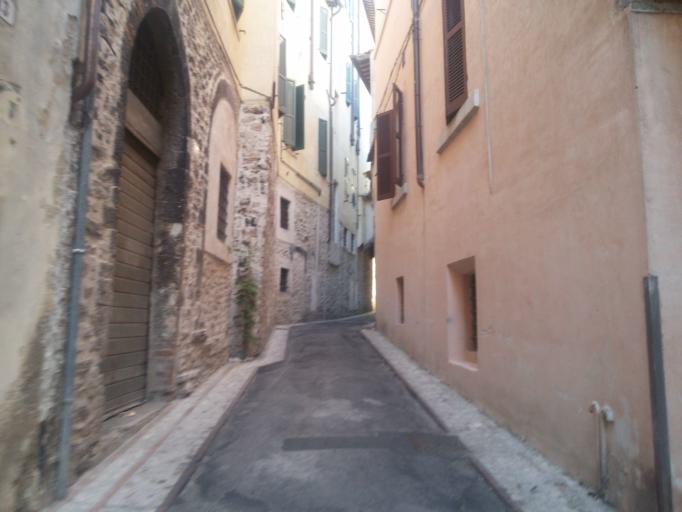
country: IT
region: Umbria
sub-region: Provincia di Perugia
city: Spoleto
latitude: 42.7336
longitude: 12.7362
